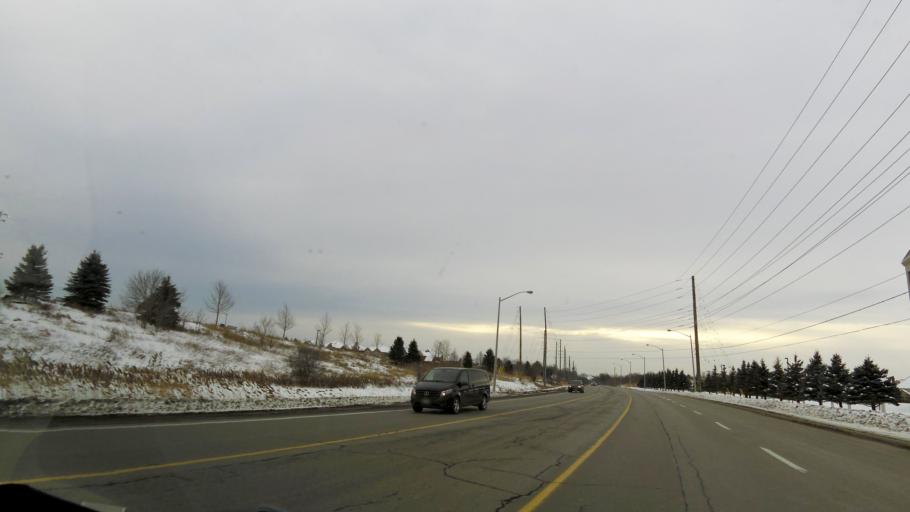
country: CA
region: Ontario
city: Vaughan
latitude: 43.8312
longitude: -79.6202
